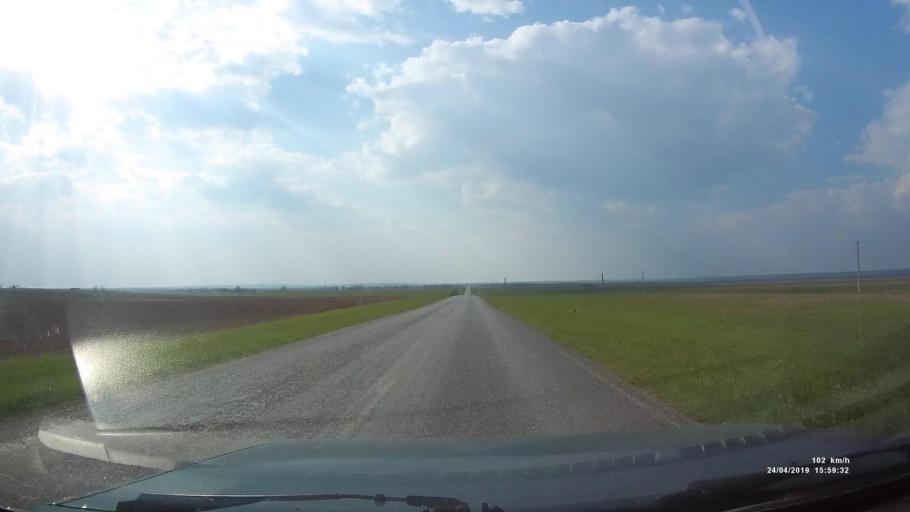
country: RU
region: Rostov
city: Sovetskoye
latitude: 46.6244
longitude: 42.4702
